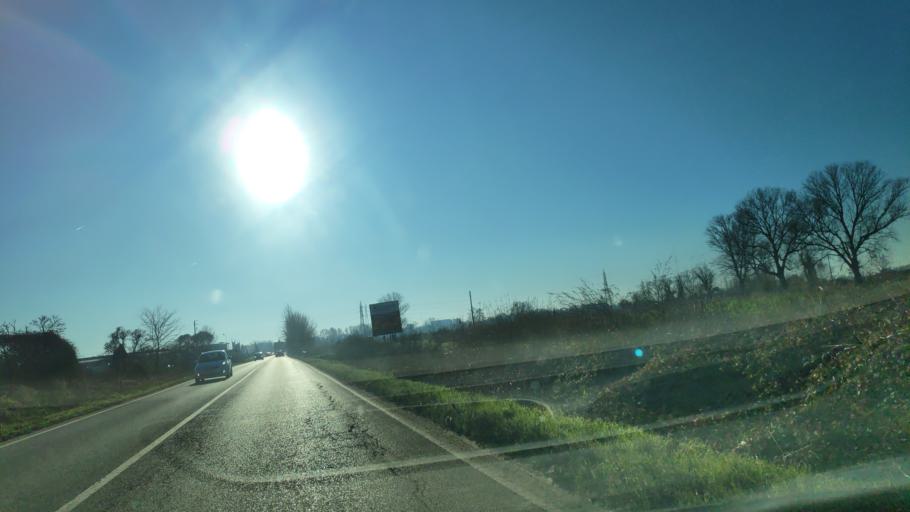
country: IT
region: Lombardy
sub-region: Citta metropolitana di Milano
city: Colturano
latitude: 45.3782
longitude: 9.3391
